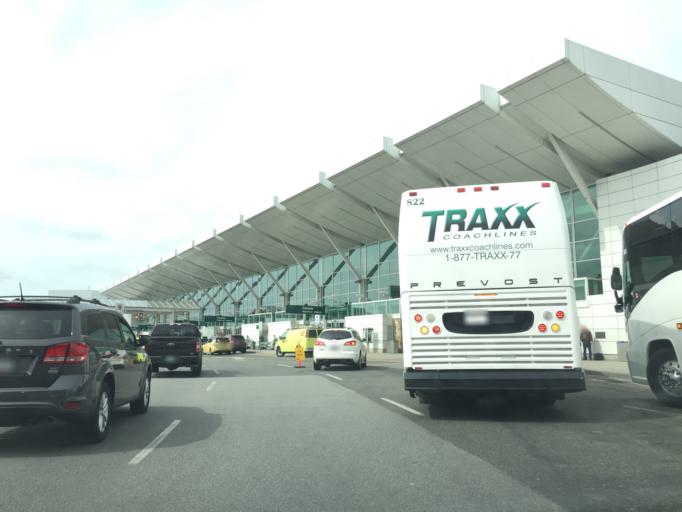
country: CA
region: British Columbia
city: Richmond
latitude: 49.1943
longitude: -123.1801
